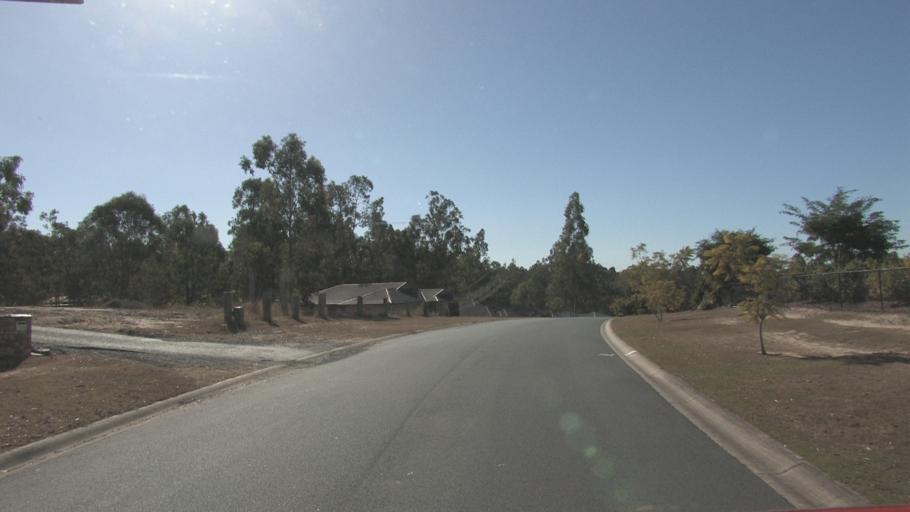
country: AU
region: Queensland
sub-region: Logan
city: Cedar Vale
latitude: -27.8655
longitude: 153.0357
